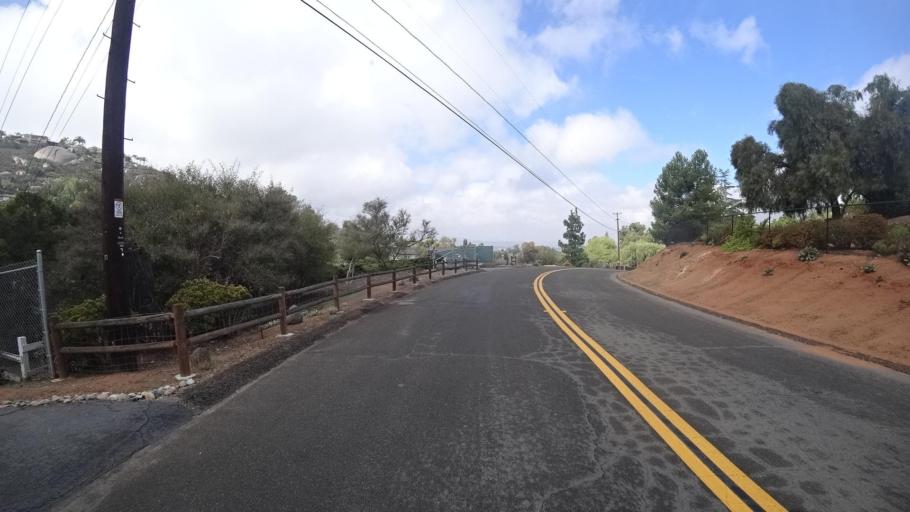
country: US
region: California
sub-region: San Diego County
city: Granite Hills
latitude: 32.7807
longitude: -116.9082
